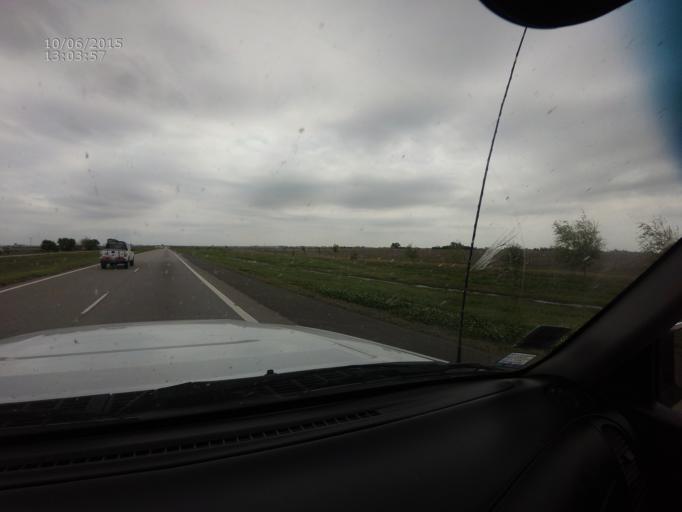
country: AR
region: Cordoba
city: General Roca
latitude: -32.7803
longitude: -61.7745
